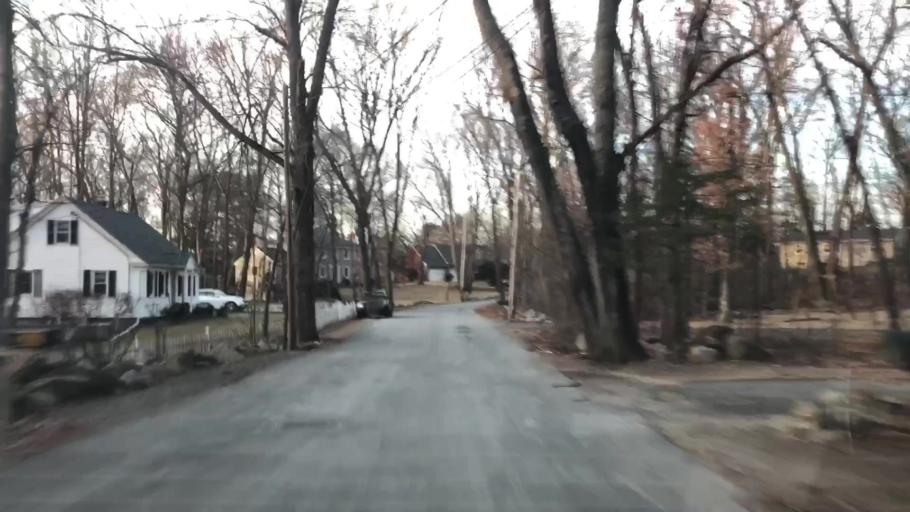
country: US
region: Massachusetts
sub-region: Essex County
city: North Andover
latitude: 42.6941
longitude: -71.0764
